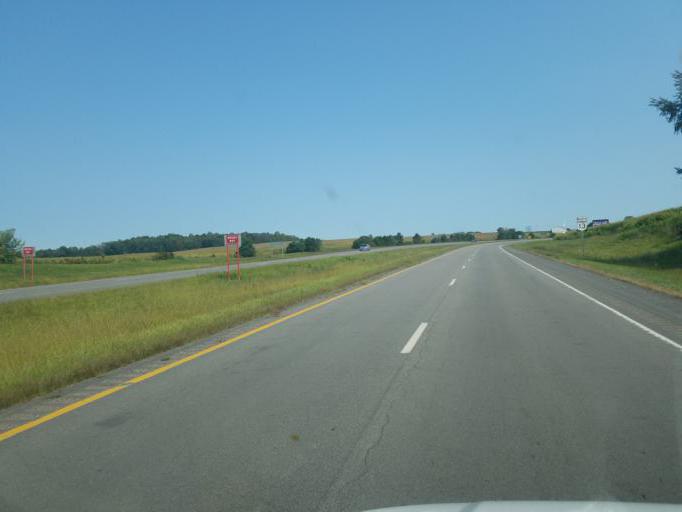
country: US
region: Ohio
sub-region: Knox County
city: Fredericktown
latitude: 40.5144
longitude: -82.5525
